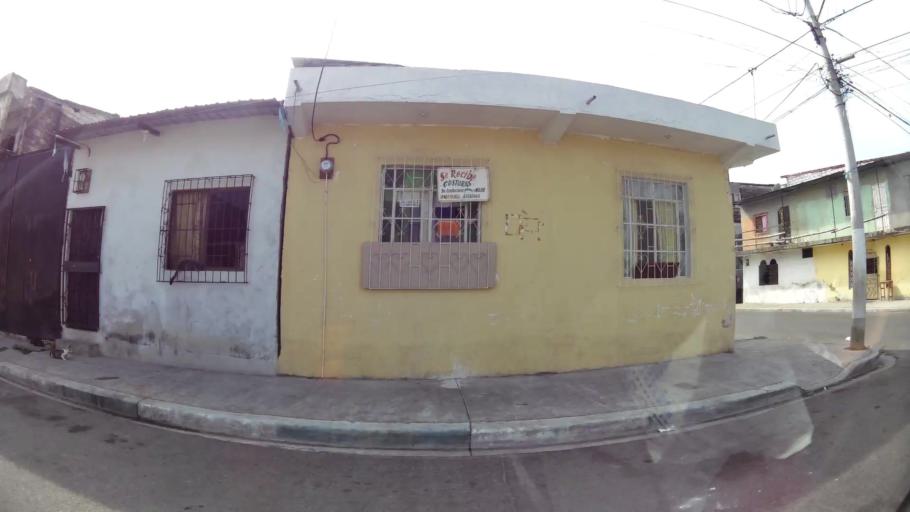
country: EC
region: Guayas
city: Guayaquil
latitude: -2.2574
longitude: -79.8811
